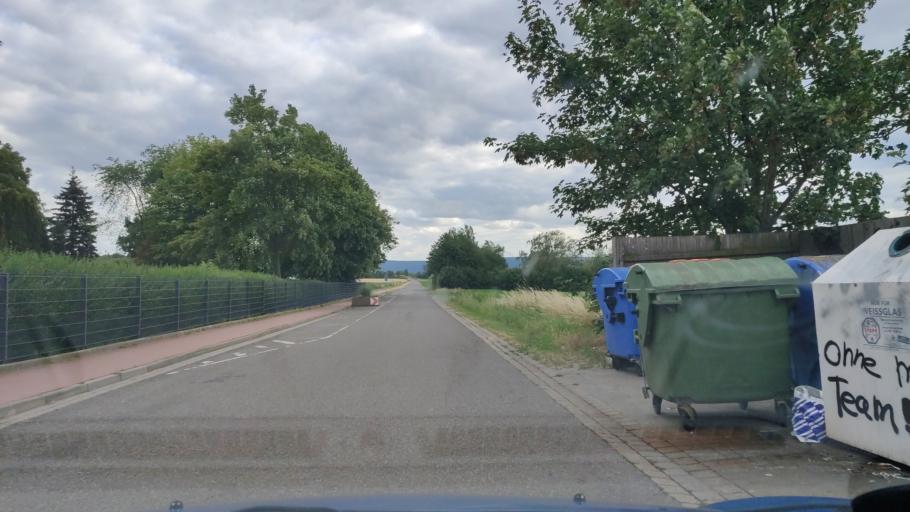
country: DE
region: Lower Saxony
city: Ronnenberg
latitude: 52.3116
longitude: 9.6502
